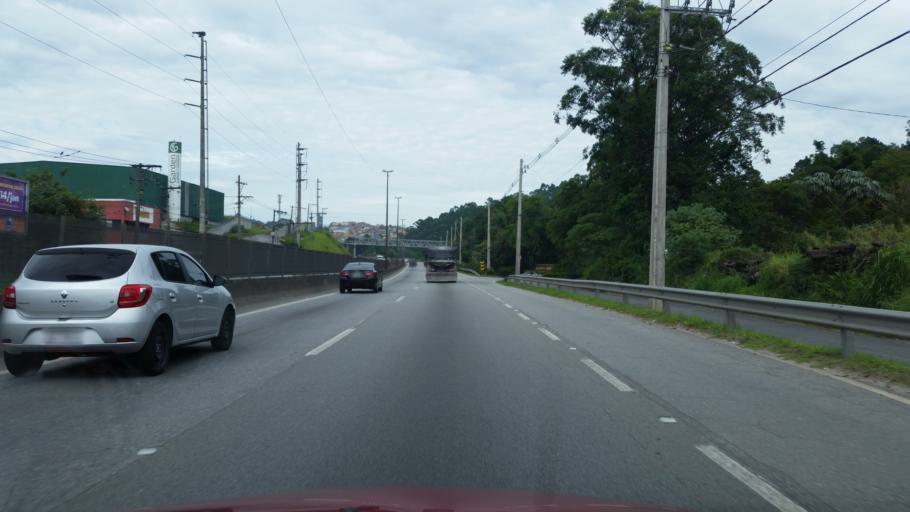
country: BR
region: Sao Paulo
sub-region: Taboao Da Serra
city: Taboao da Serra
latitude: -23.6179
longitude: -46.8050
